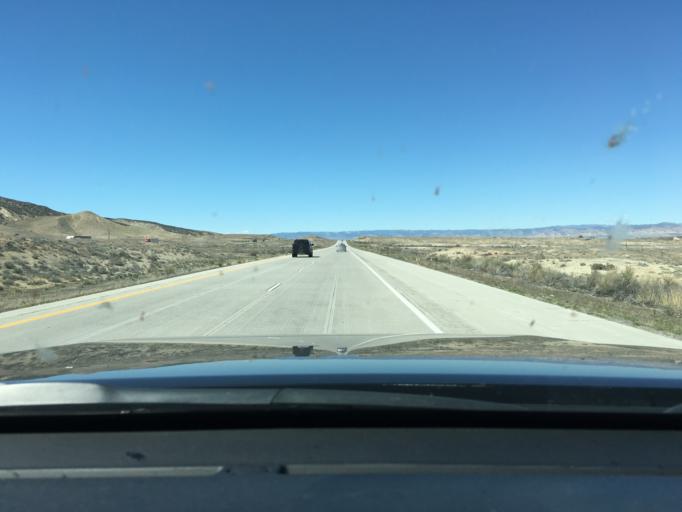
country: US
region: Colorado
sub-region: Mesa County
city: Loma
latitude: 39.1856
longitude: -108.8318
